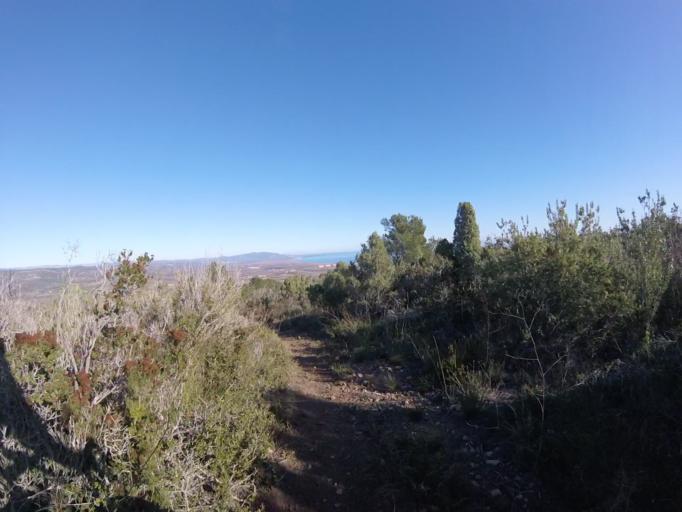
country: ES
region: Valencia
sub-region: Provincia de Castello
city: Orpesa/Oropesa del Mar
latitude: 40.1066
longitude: 0.1172
